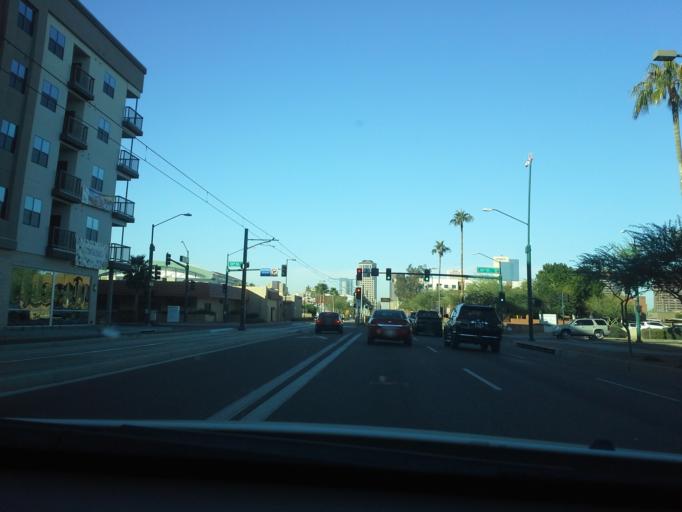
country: US
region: Arizona
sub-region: Maricopa County
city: Phoenix
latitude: 33.4483
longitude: -112.0558
